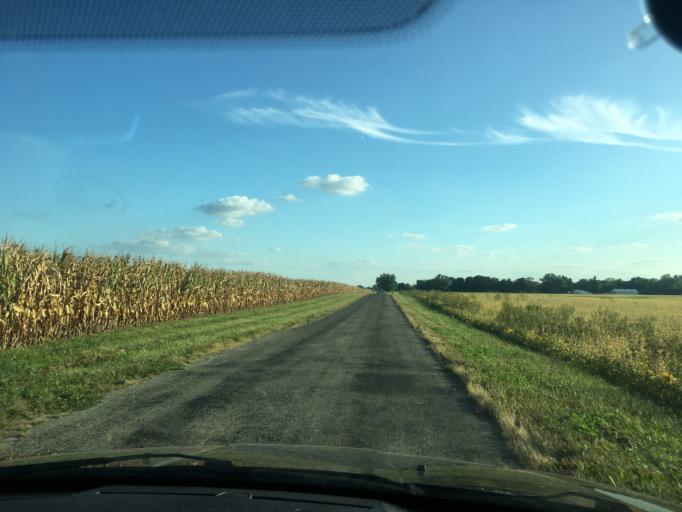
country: US
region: Ohio
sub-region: Logan County
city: West Liberty
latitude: 40.2149
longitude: -83.7396
